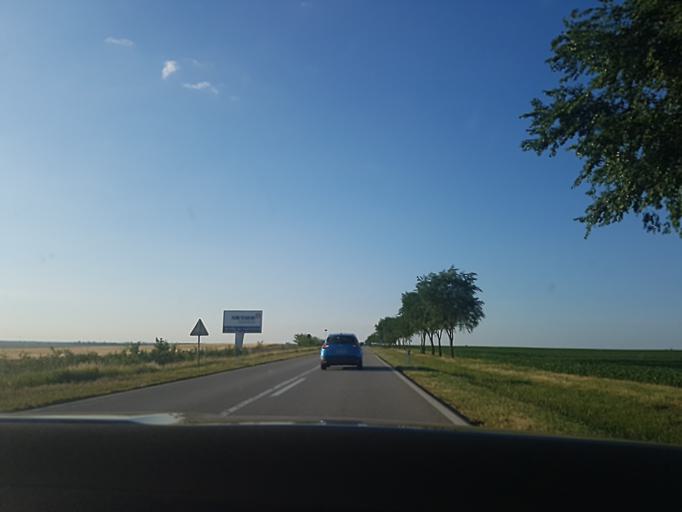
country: RO
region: Timis
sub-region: Comuna Moravita
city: Moravita
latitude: 45.1982
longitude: 21.3000
